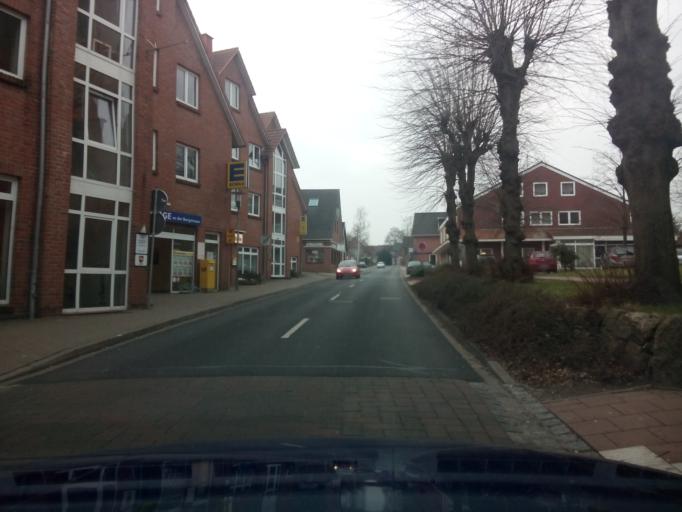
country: DE
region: Lower Saxony
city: Lintig
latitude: 53.6246
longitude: 8.8415
